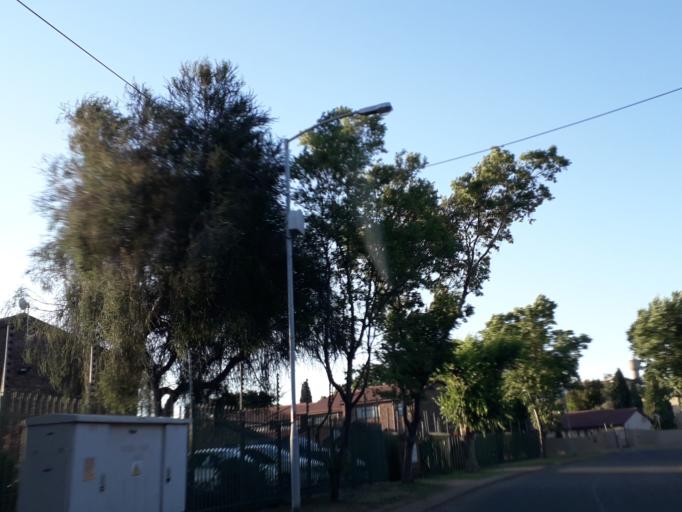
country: ZA
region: Gauteng
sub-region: City of Johannesburg Metropolitan Municipality
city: Roodepoort
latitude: -26.1601
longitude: 27.9459
